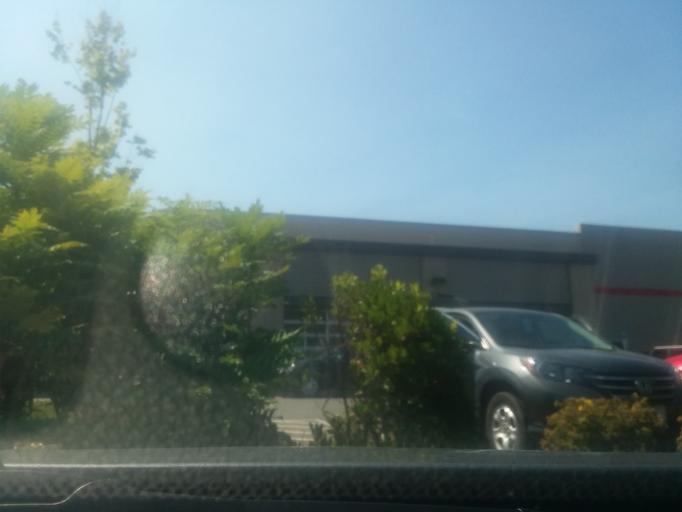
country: CA
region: British Columbia
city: Courtenay
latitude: 49.7141
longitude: -124.9634
